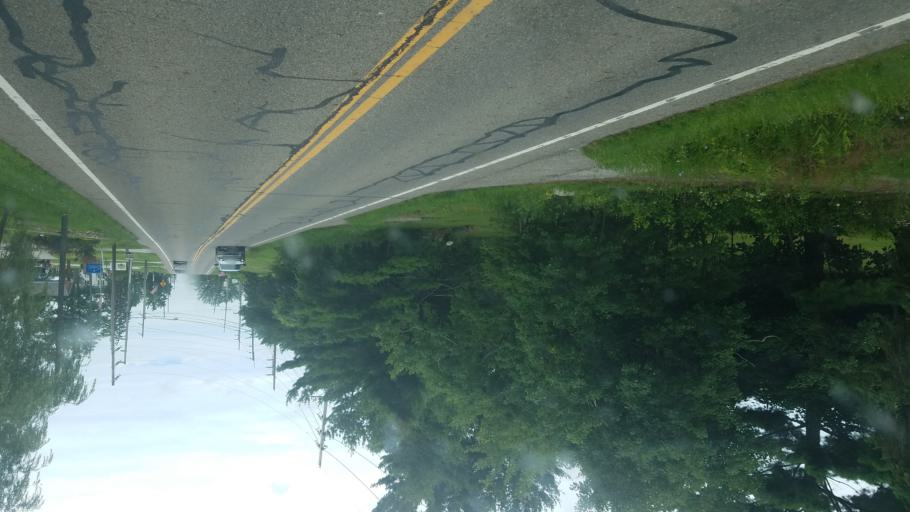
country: US
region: Ohio
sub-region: Geauga County
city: Burton
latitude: 41.4597
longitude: -81.2444
